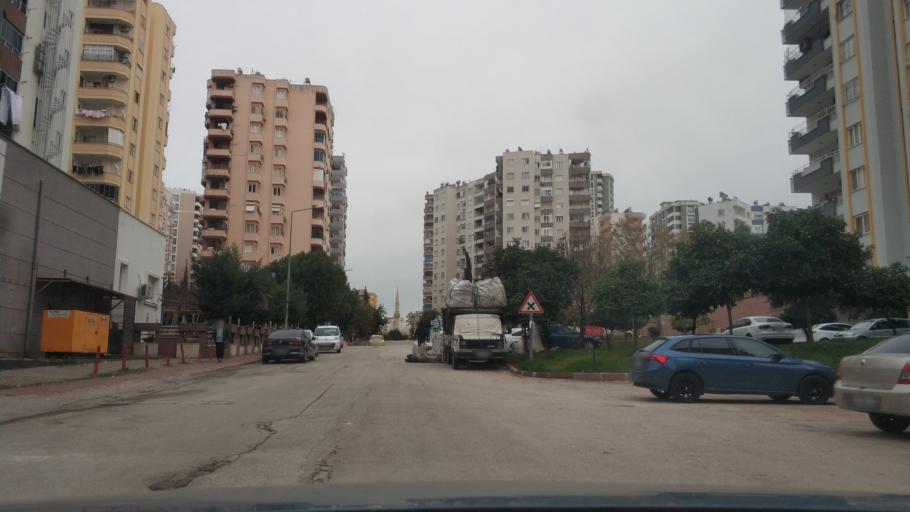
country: TR
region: Adana
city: Seyhan
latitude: 37.0551
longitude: 35.2787
